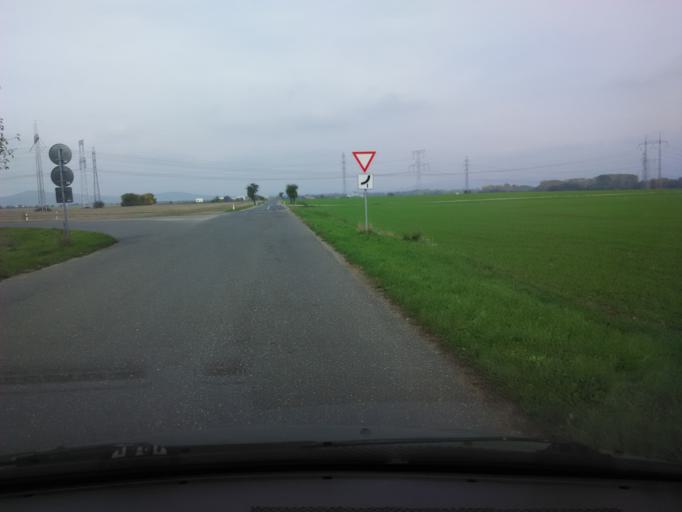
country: SK
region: Nitriansky
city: Tlmace
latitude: 48.2132
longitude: 18.5193
